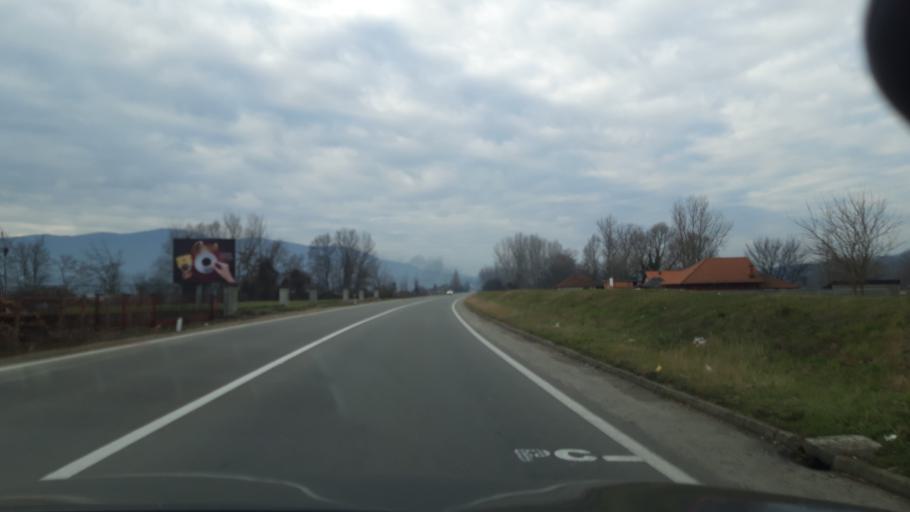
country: RS
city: Lipnicki Sor
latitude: 44.5507
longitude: 19.1972
